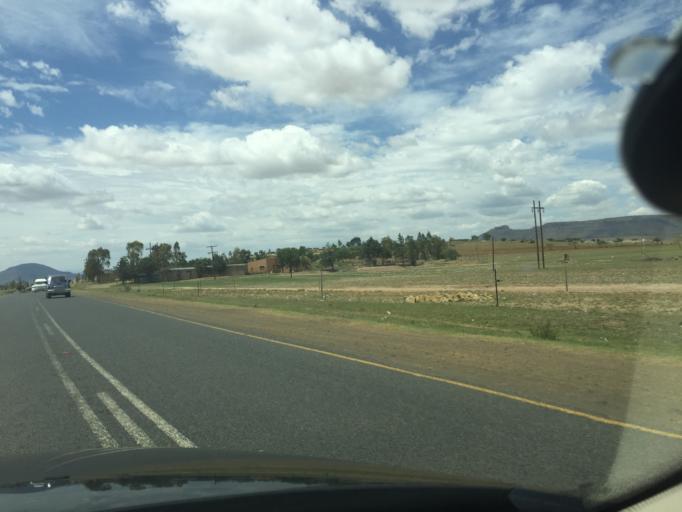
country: LS
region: Mafeteng
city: Mafeteng
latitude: -29.9796
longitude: 27.3225
